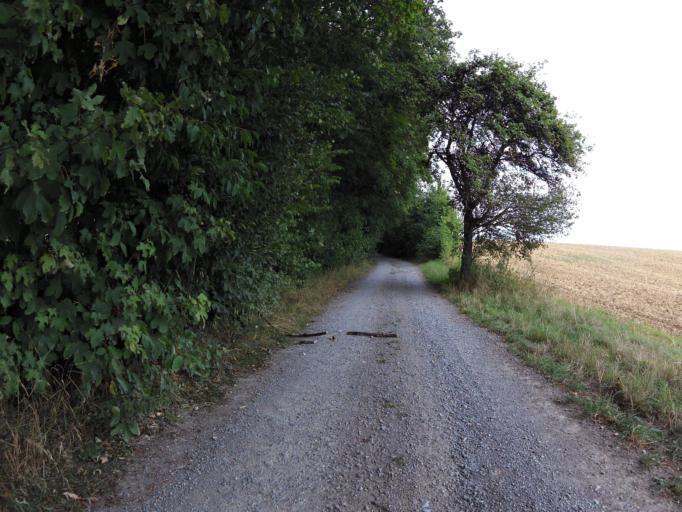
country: DE
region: Bavaria
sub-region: Regierungsbezirk Unterfranken
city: Kleinrinderfeld
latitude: 49.7041
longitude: 9.8290
